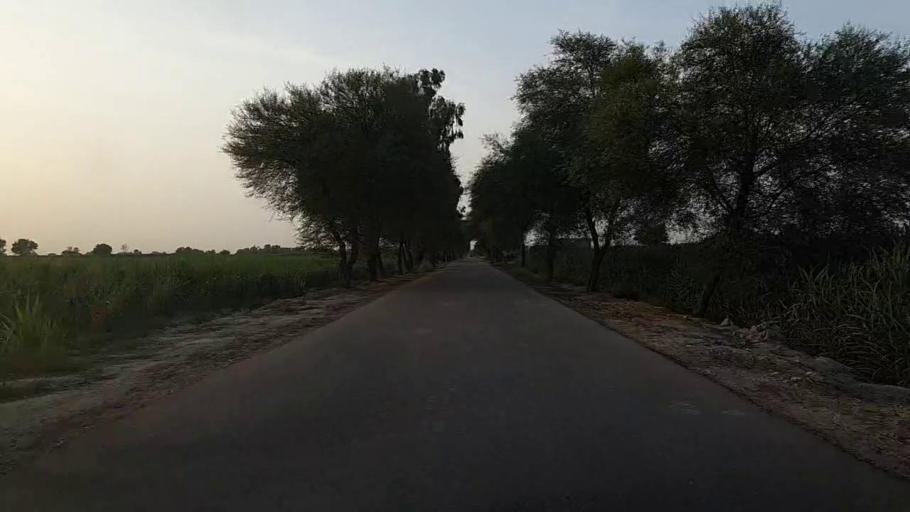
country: PK
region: Sindh
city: Ubauro
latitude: 28.2463
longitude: 69.8097
